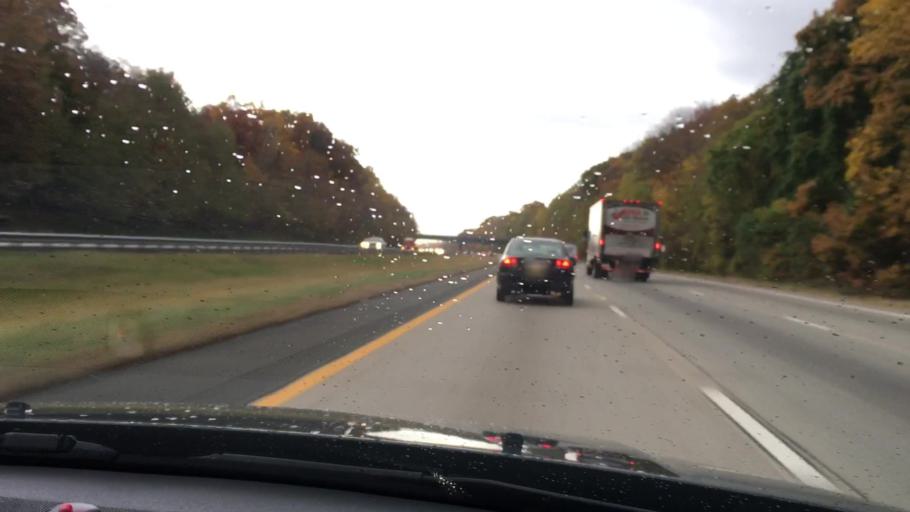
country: US
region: New Jersey
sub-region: Bergen County
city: Ramsey
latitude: 41.0633
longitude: -74.1833
